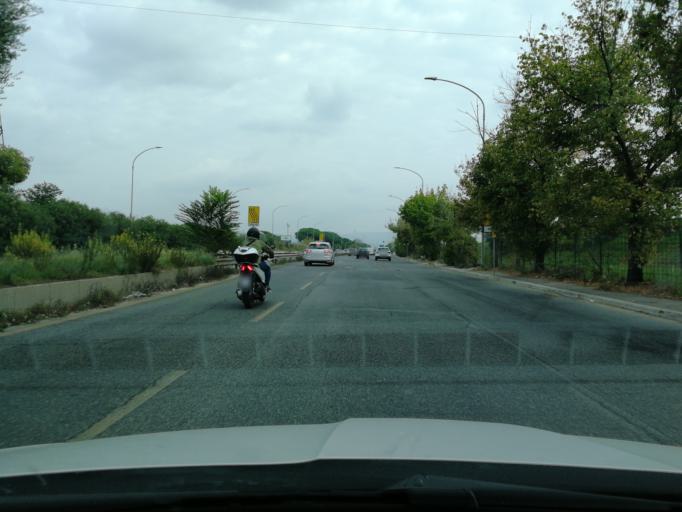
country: IT
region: Latium
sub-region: Citta metropolitana di Roma Capitale
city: Ciampino
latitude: 41.8479
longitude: 12.5764
